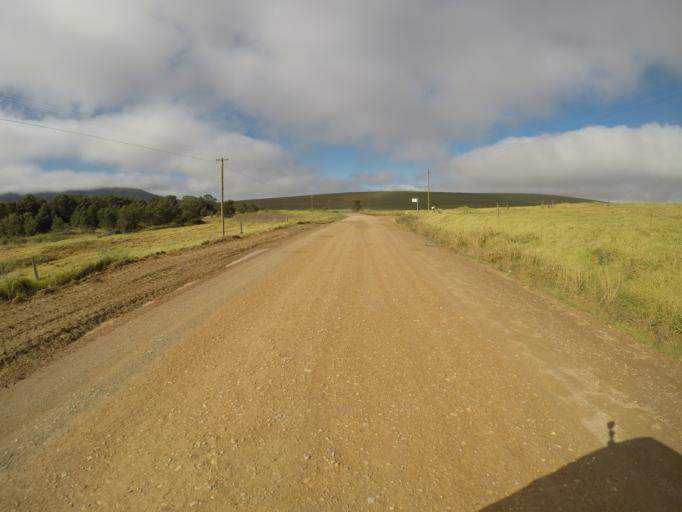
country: ZA
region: Western Cape
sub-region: Cape Winelands District Municipality
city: Ashton
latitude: -34.1295
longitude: 19.8447
